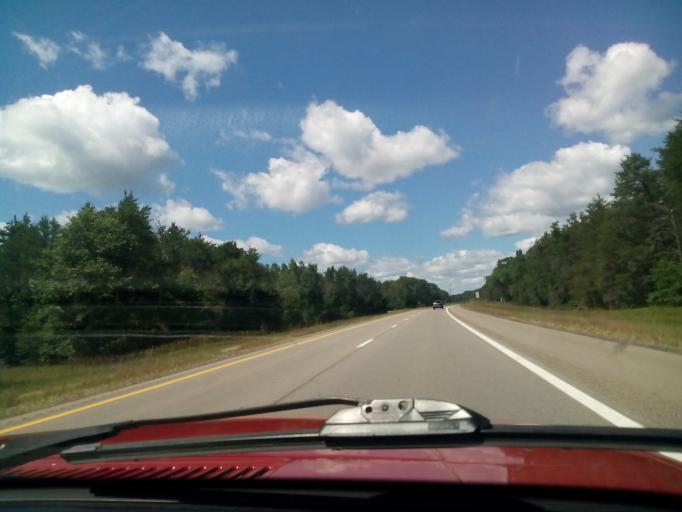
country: US
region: Michigan
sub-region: Roscommon County
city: Roscommon
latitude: 44.4650
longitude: -84.6117
